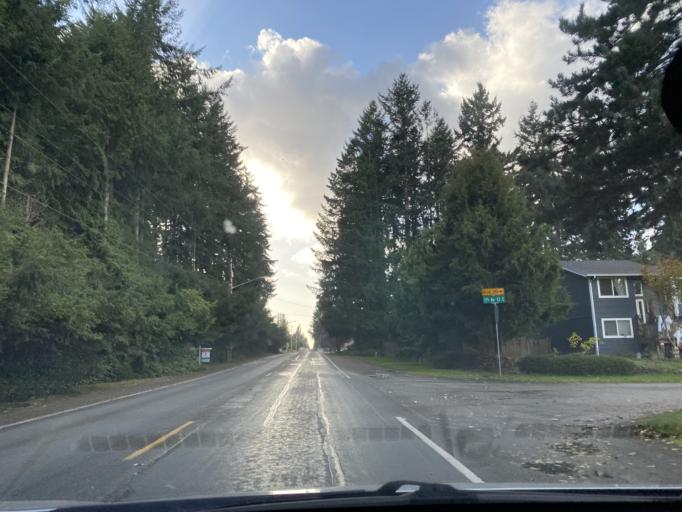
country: US
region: Washington
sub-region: Pierce County
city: South Hill
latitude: 47.1184
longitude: -122.2751
